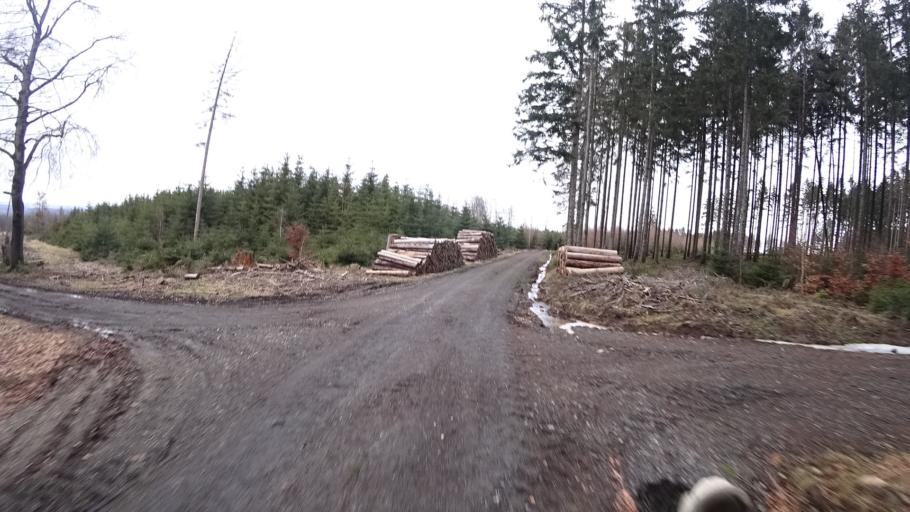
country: DE
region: Rheinland-Pfalz
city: Ransbach-Baumbach
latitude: 50.4309
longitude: 7.7272
